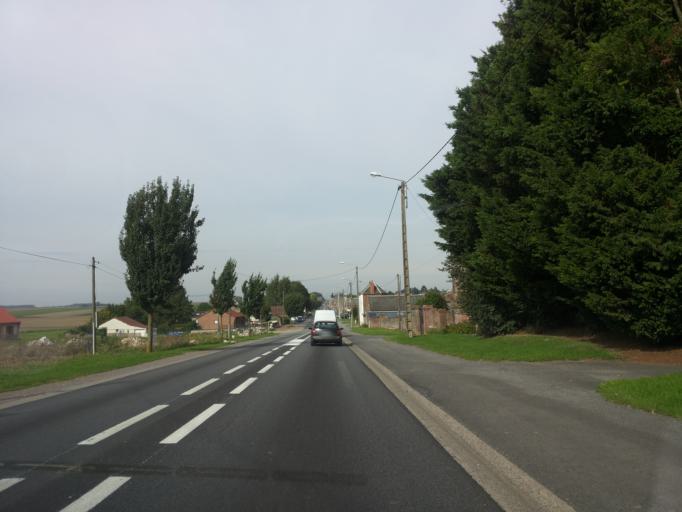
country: FR
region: Nord-Pas-de-Calais
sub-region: Departement du Nord
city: Raillencourt-Sainte-Olle
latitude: 50.1862
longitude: 3.1847
